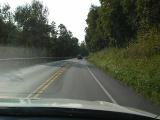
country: US
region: Pennsylvania
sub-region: Potter County
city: Coudersport
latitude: 41.7523
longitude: -78.1040
